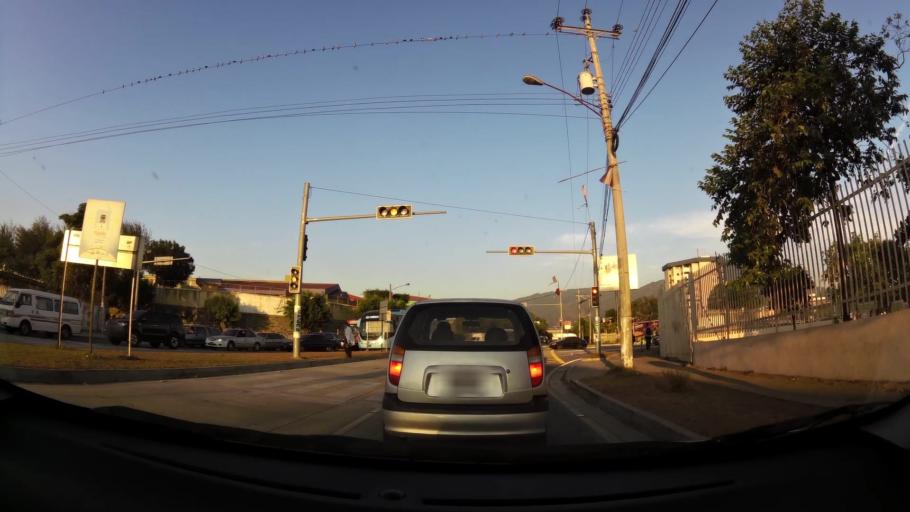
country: SV
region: San Salvador
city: San Salvador
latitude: 13.7029
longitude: -89.2080
